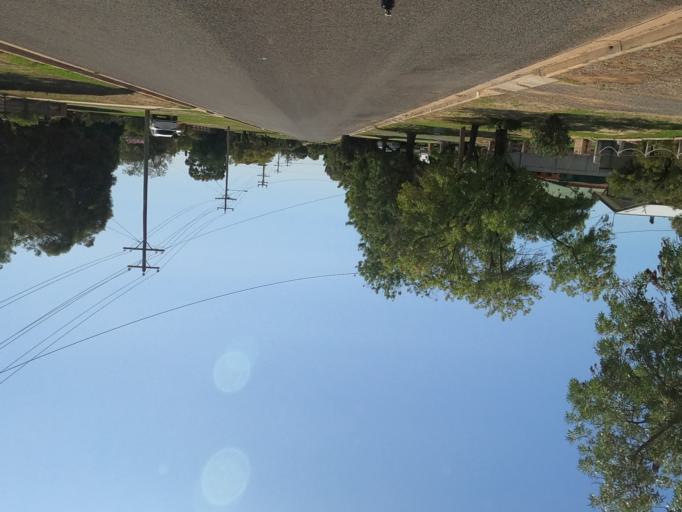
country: AU
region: New South Wales
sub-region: Corowa Shire
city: Mulwala
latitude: -35.9854
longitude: 146.0073
